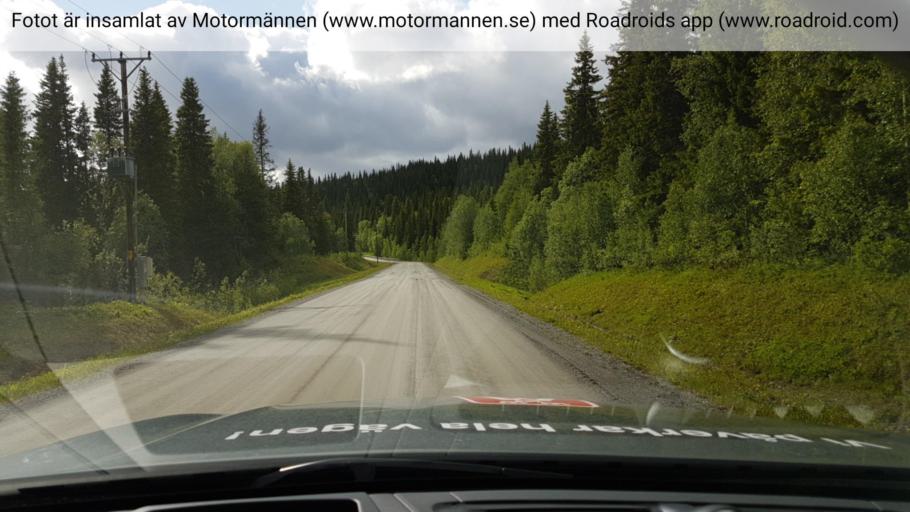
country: SE
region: Jaemtland
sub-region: Are Kommun
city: Are
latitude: 63.7051
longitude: 12.7495
